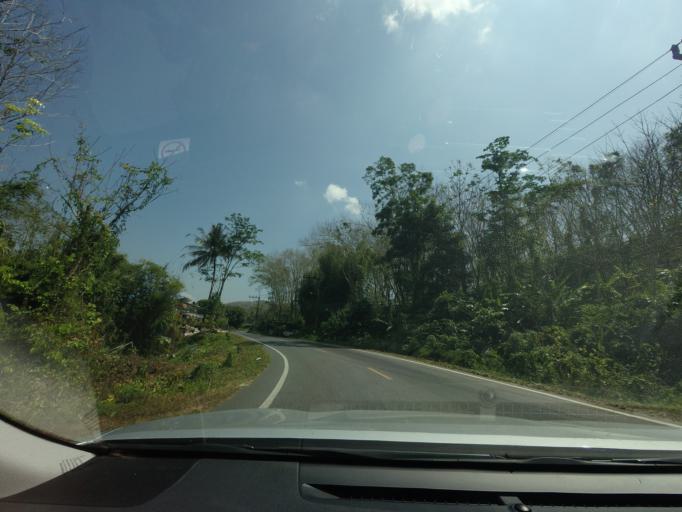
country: TH
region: Phangnga
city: Takua Thung
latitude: 8.2477
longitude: 98.3917
